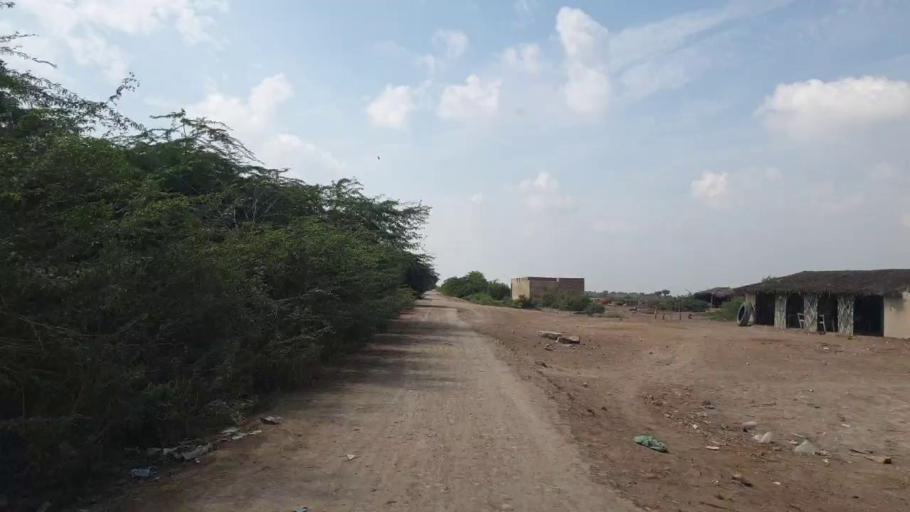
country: PK
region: Sindh
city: Badin
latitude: 24.5066
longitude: 68.6436
